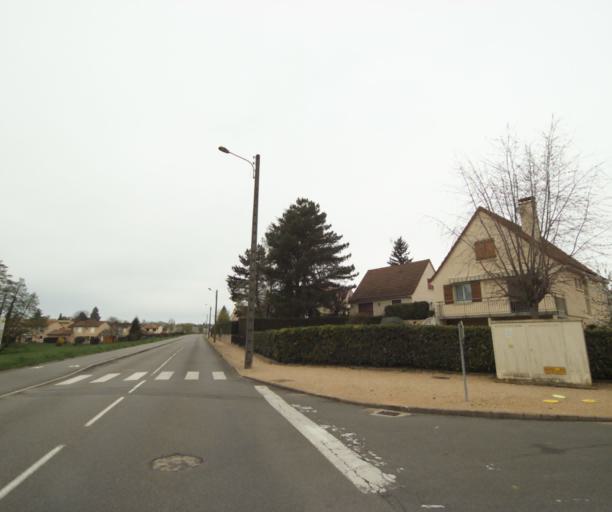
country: FR
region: Bourgogne
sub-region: Departement de Saone-et-Loire
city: Charnay-les-Macon
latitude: 46.3033
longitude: 4.8069
